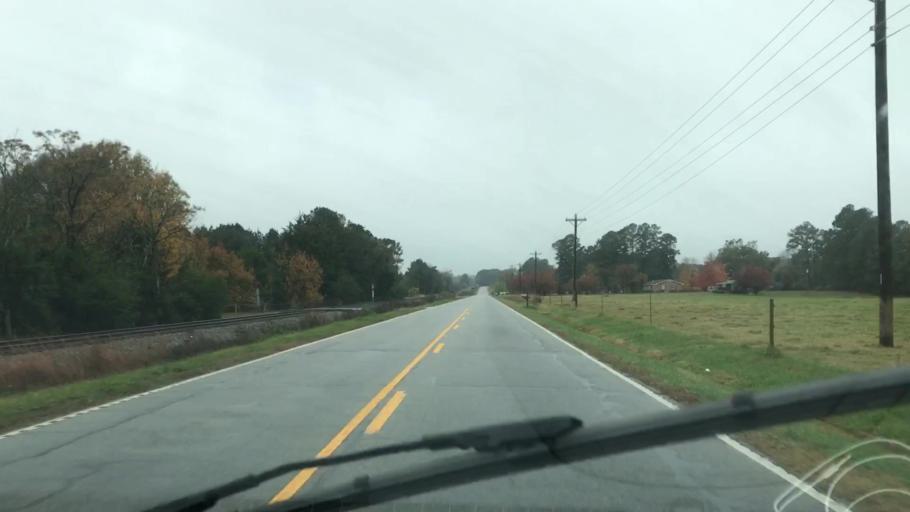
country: US
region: South Carolina
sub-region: Newberry County
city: Newberry
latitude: 34.3493
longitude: -81.6958
